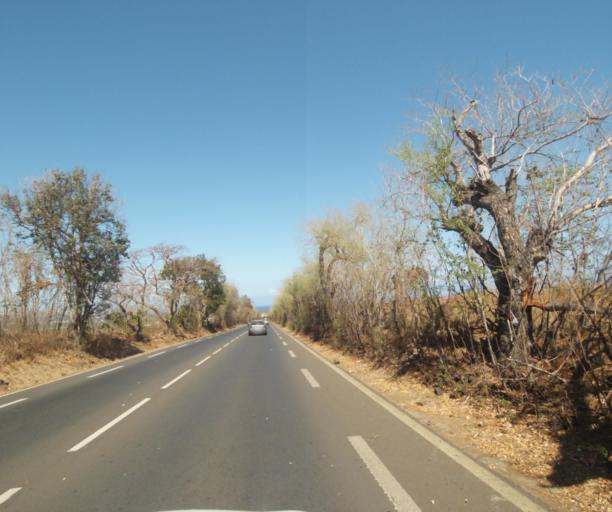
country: RE
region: Reunion
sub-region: Reunion
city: Le Port
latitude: -20.9814
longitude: 55.3116
